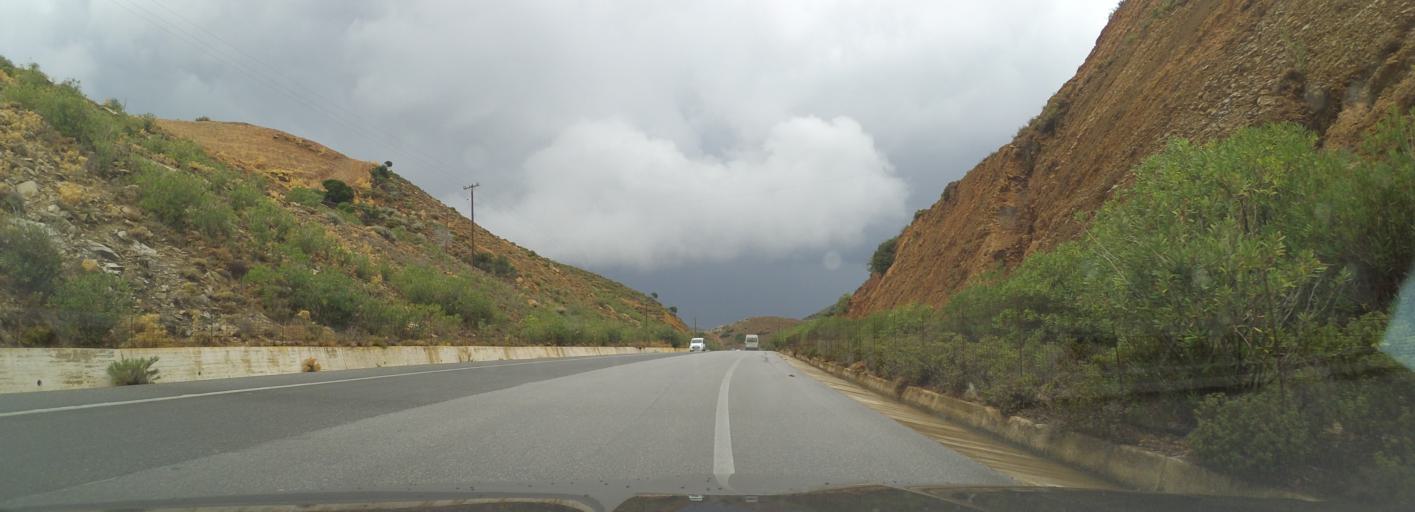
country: GR
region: Crete
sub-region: Nomos Rethymnis
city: Anogeia
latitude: 35.3908
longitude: 24.9289
